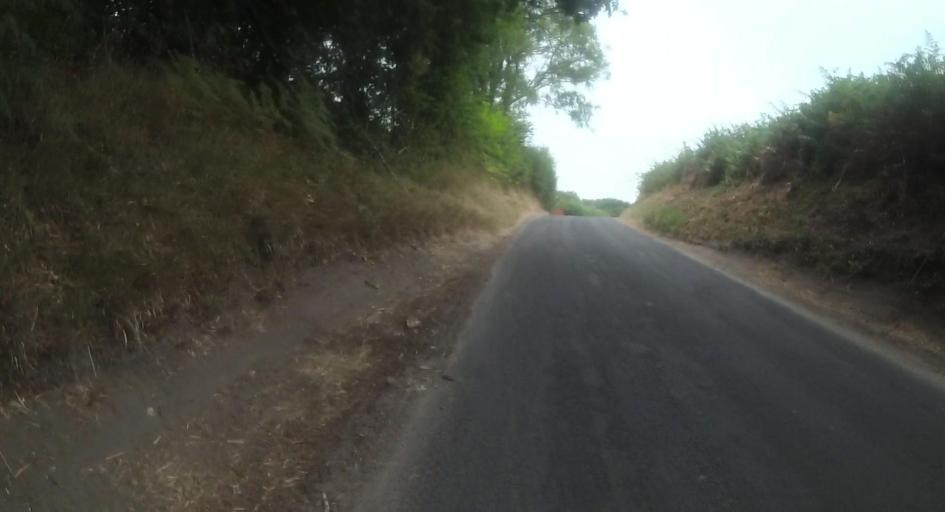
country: GB
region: England
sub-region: Dorset
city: Wareham
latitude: 50.6431
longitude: -2.0966
